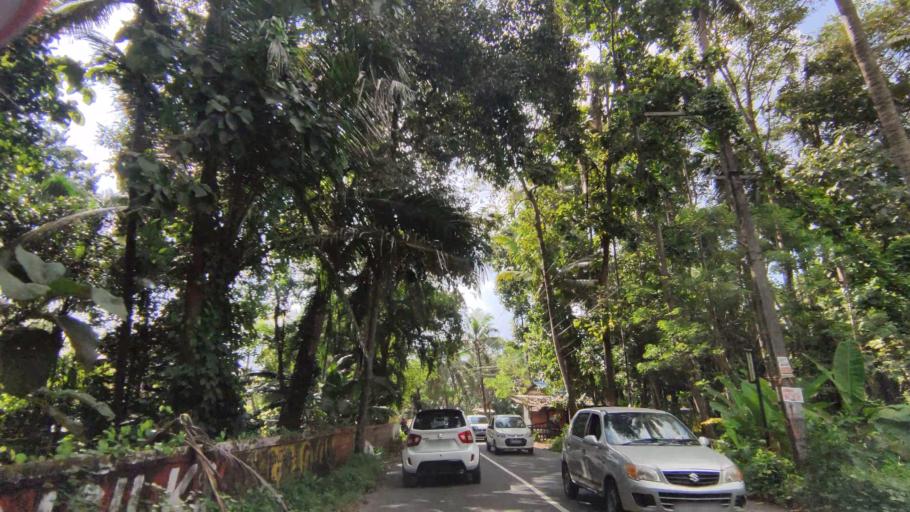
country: IN
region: Kerala
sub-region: Kottayam
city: Kottayam
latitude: 9.6897
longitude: 76.4983
